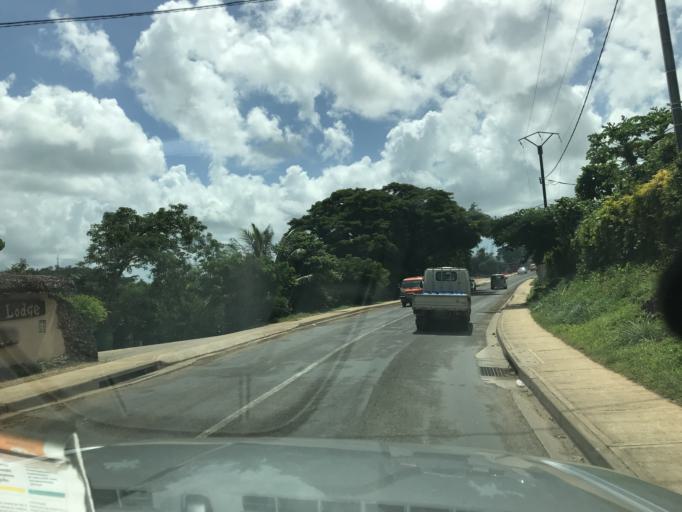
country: VU
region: Shefa
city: Port-Vila
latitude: -17.7252
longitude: 168.3109
